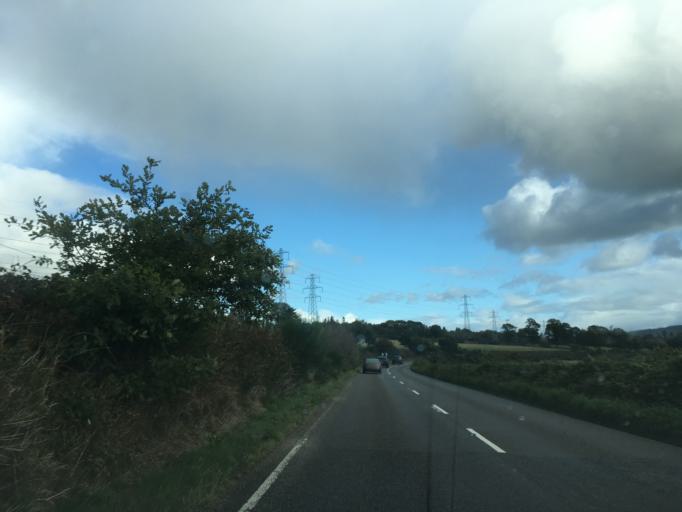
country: GB
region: Scotland
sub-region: Highland
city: Beauly
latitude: 57.4684
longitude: -4.4312
